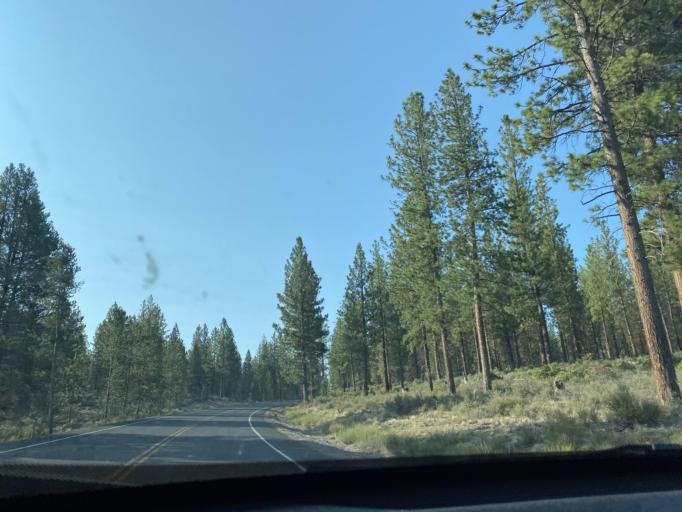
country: US
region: Oregon
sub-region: Deschutes County
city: La Pine
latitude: 43.7249
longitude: -121.4154
